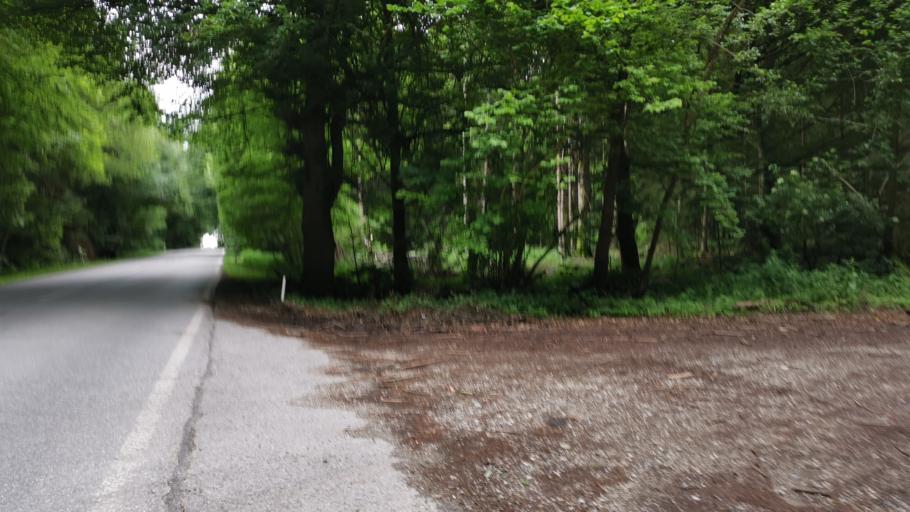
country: DE
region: Bavaria
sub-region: Upper Bavaria
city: Schaftlarn
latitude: 48.0070
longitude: 11.4250
